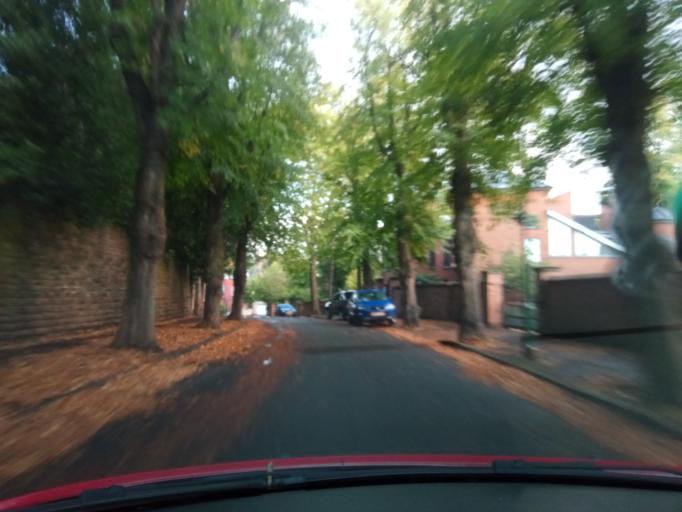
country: GB
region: England
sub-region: Nottingham
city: Nottingham
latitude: 52.9710
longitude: -1.1473
